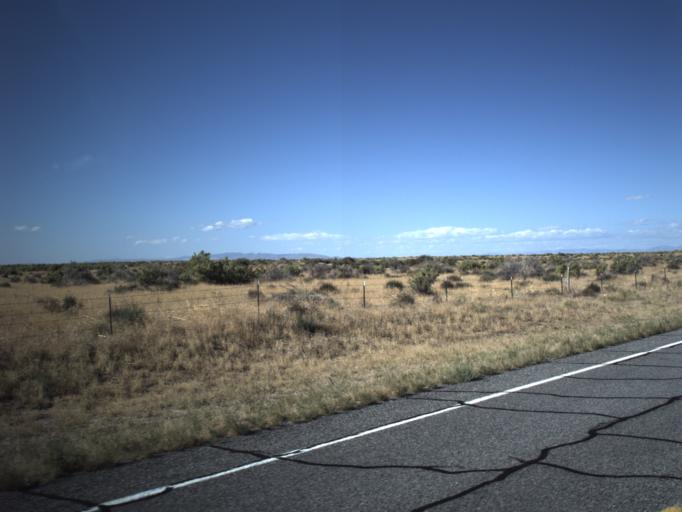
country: US
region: Utah
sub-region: Millard County
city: Delta
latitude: 39.3536
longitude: -112.4613
